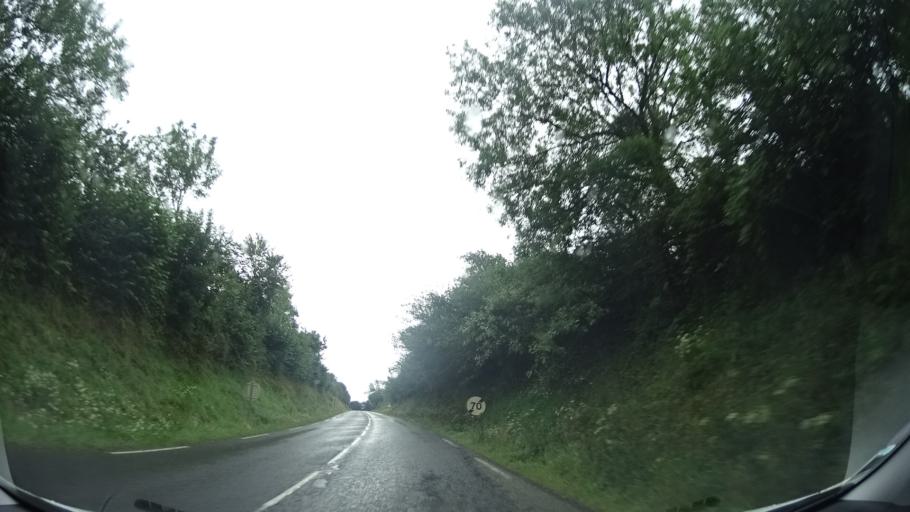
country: FR
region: Lower Normandy
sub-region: Departement de la Manche
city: Beaumont-Hague
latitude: 49.6068
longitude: -1.7894
